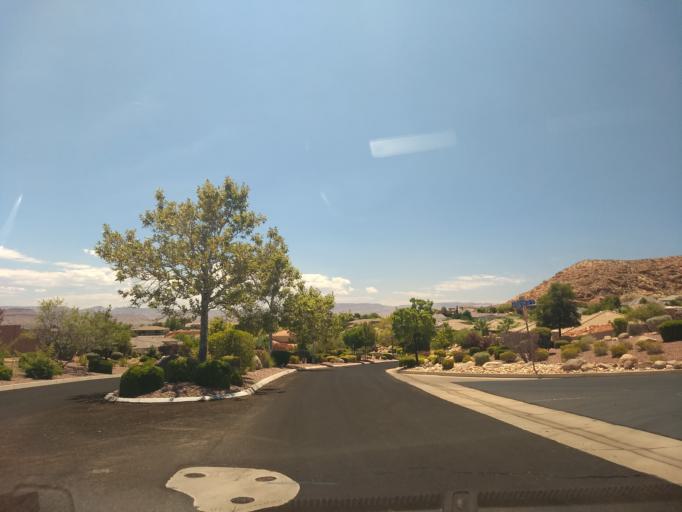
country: US
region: Utah
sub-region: Washington County
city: Washington
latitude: 37.1513
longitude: -113.5305
